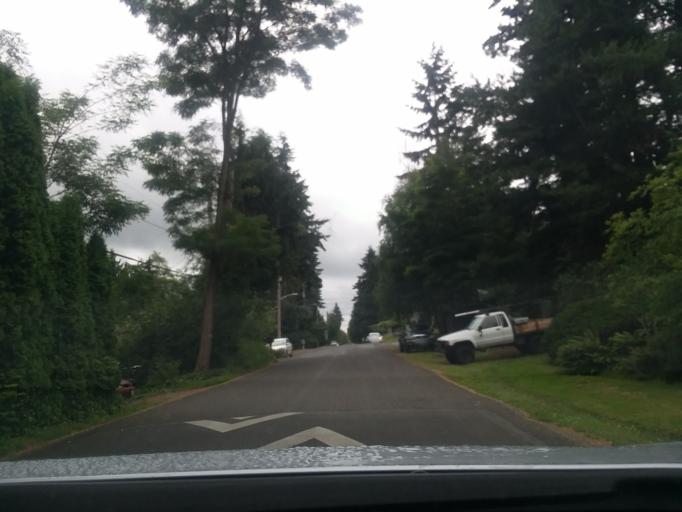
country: US
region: Washington
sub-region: King County
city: Lake Forest Park
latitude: 47.7279
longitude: -122.2992
